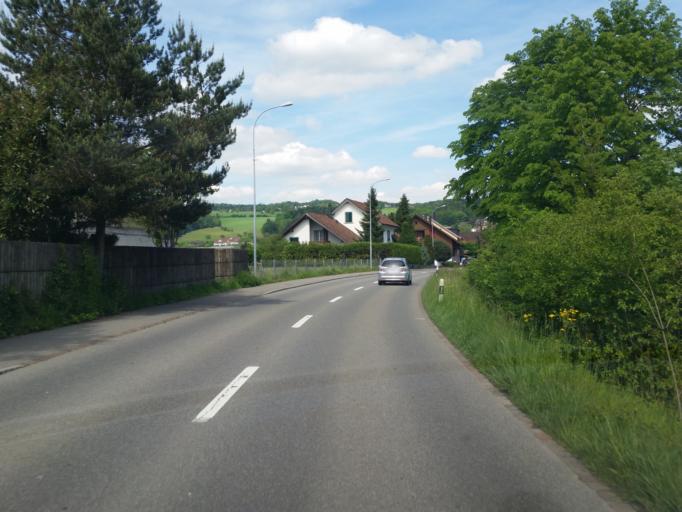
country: CH
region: Aargau
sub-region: Bezirk Bremgarten
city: Unterlunkhofen
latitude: 47.3181
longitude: 8.3694
